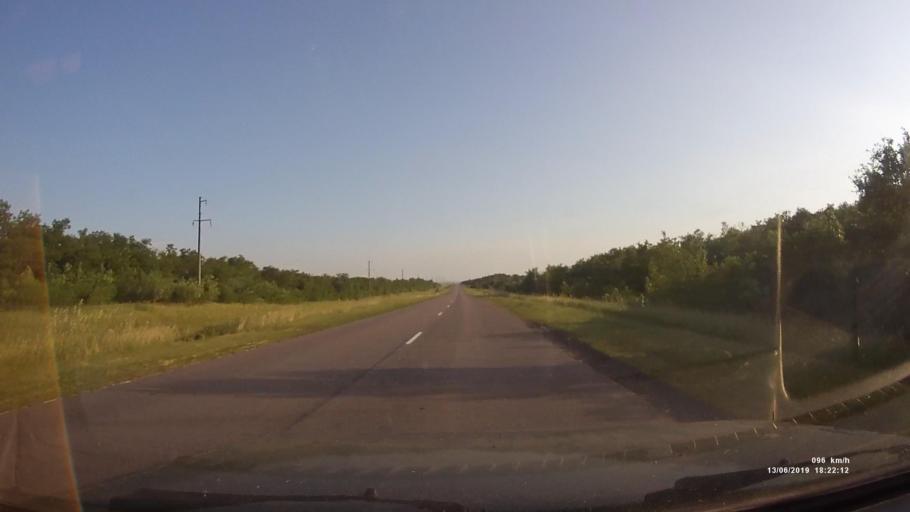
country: RU
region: Rostov
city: Kazanskaya
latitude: 49.8617
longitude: 41.2809
